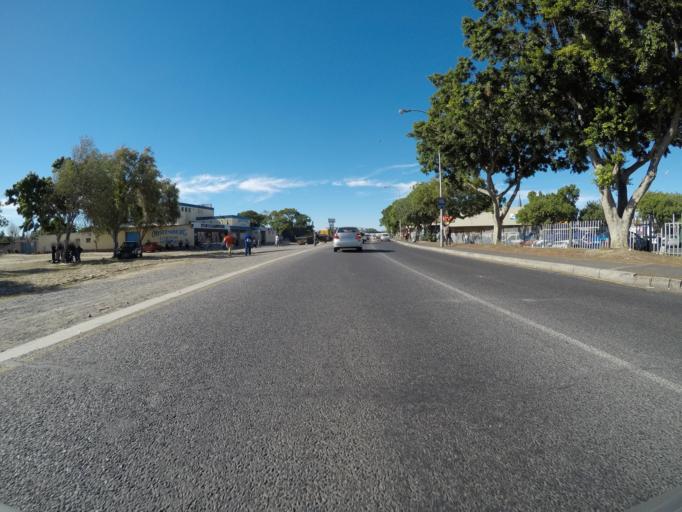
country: ZA
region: Western Cape
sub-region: City of Cape Town
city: Kraaifontein
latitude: -33.9260
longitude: 18.6766
